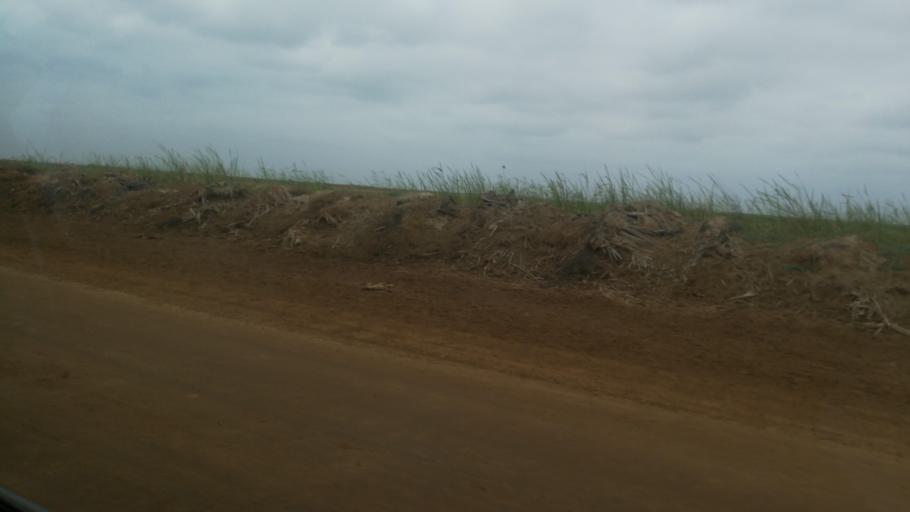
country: SN
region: Saint-Louis
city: Saint-Louis
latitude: 16.3167
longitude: -16.2337
